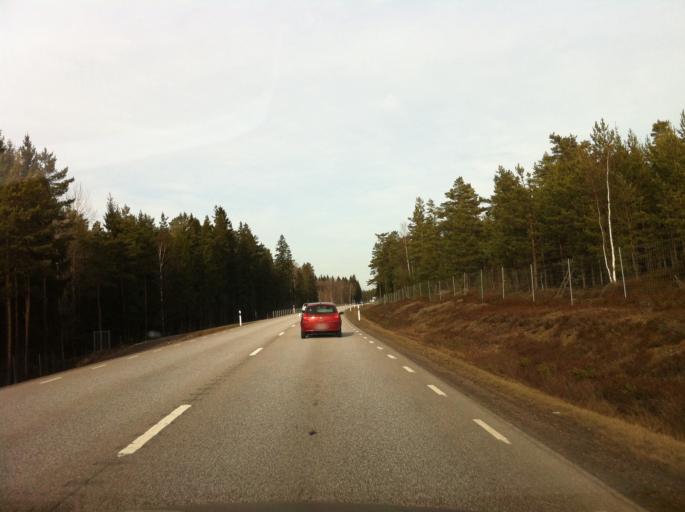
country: SE
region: Vaestra Goetaland
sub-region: Gullspangs Kommun
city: Gullspang
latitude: 58.9155
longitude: 14.0269
